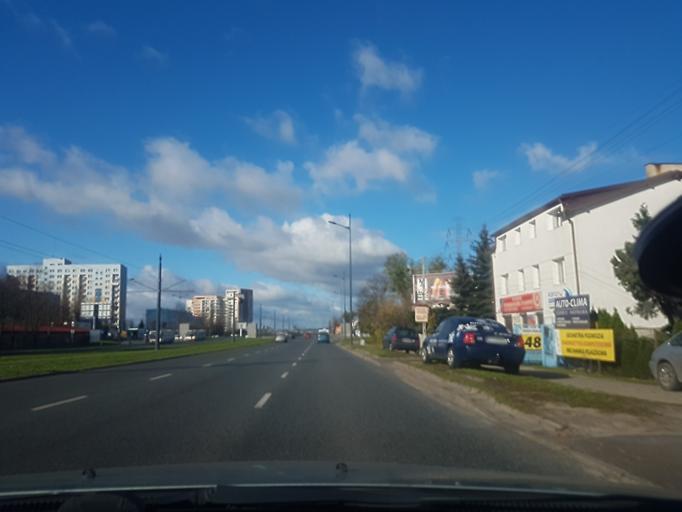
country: PL
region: Lodz Voivodeship
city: Lodz
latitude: 51.7621
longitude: 19.5306
